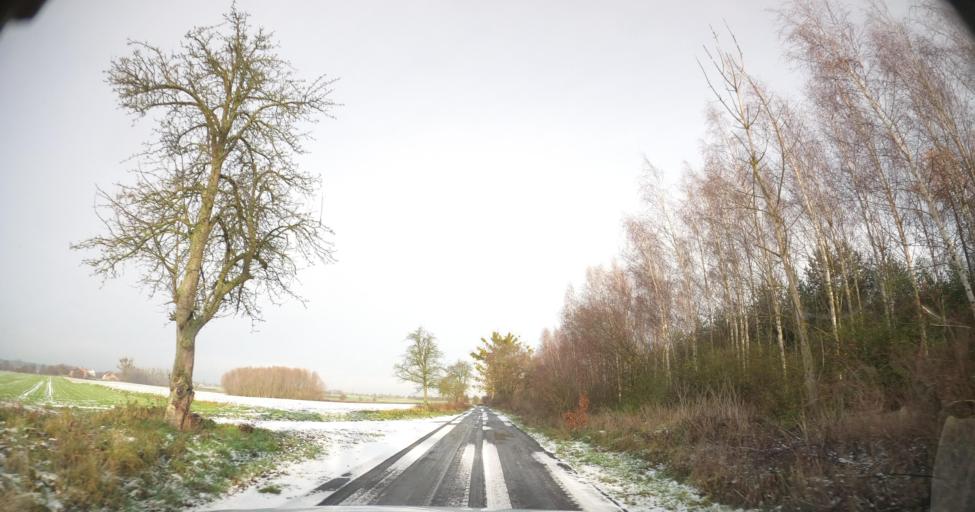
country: PL
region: West Pomeranian Voivodeship
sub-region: Powiat gryfinski
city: Mieszkowice
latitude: 52.7685
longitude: 14.4876
